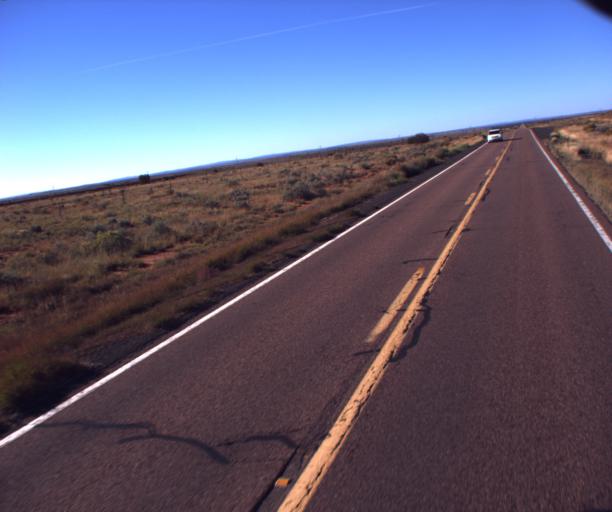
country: US
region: Arizona
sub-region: Navajo County
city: Heber-Overgaard
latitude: 34.6262
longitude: -110.3655
